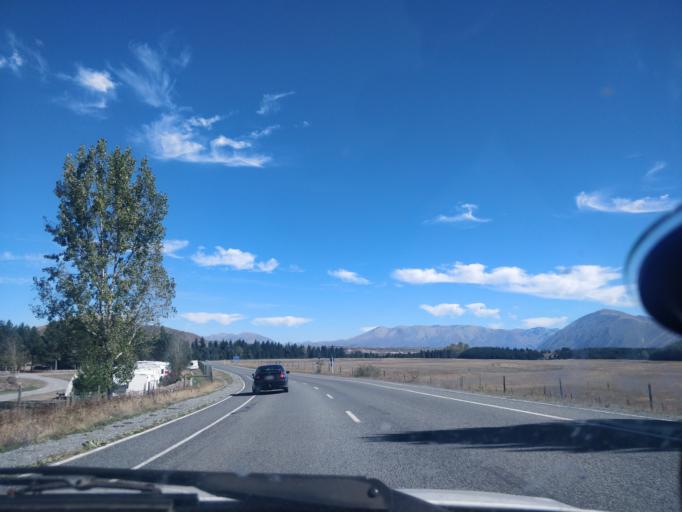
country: NZ
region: Otago
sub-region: Queenstown-Lakes District
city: Wanaka
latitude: -44.2696
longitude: 170.0649
